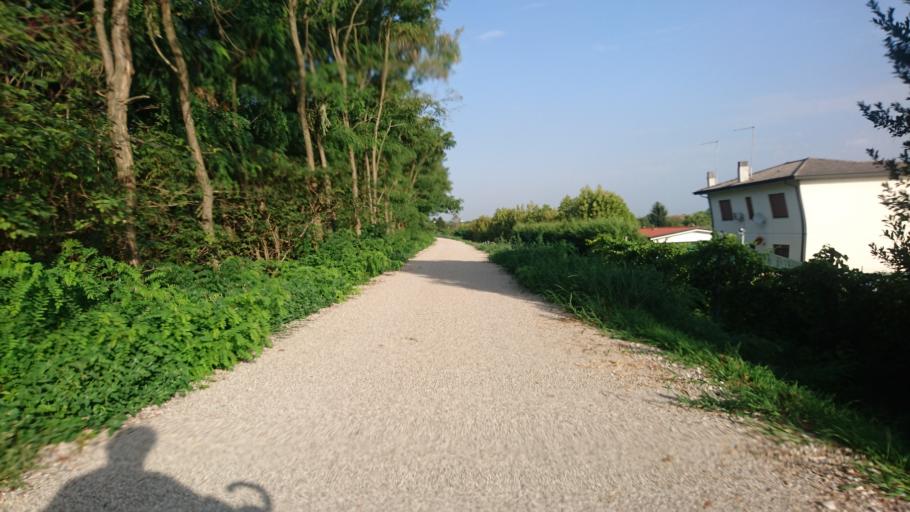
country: IT
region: Veneto
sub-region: Provincia di Padova
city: Cadoneghe
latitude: 45.4369
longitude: 11.9383
